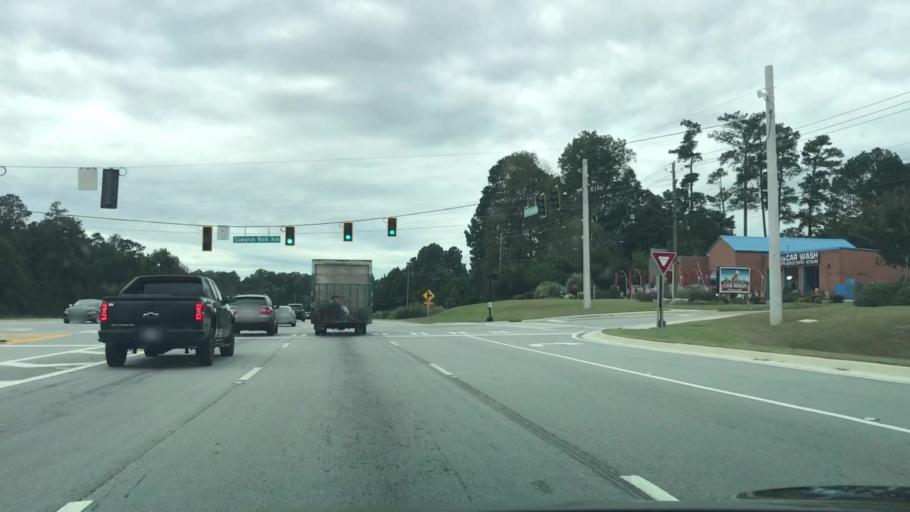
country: US
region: Georgia
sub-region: Gwinnett County
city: Suwanee
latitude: 34.0479
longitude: -84.0937
